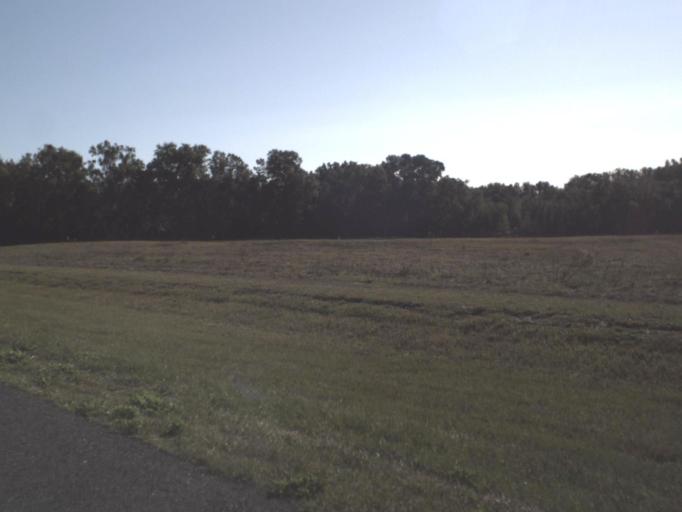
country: US
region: Florida
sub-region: Marion County
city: Belleview
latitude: 29.0292
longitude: -82.0599
